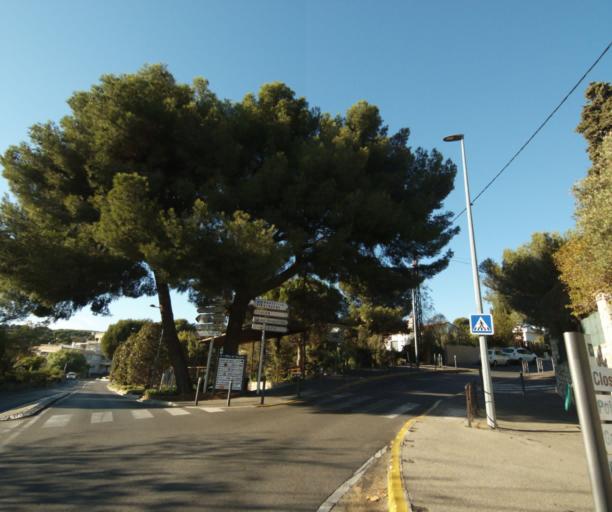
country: FR
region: Provence-Alpes-Cote d'Azur
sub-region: Departement des Bouches-du-Rhone
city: Cassis
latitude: 43.2180
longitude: 5.5406
